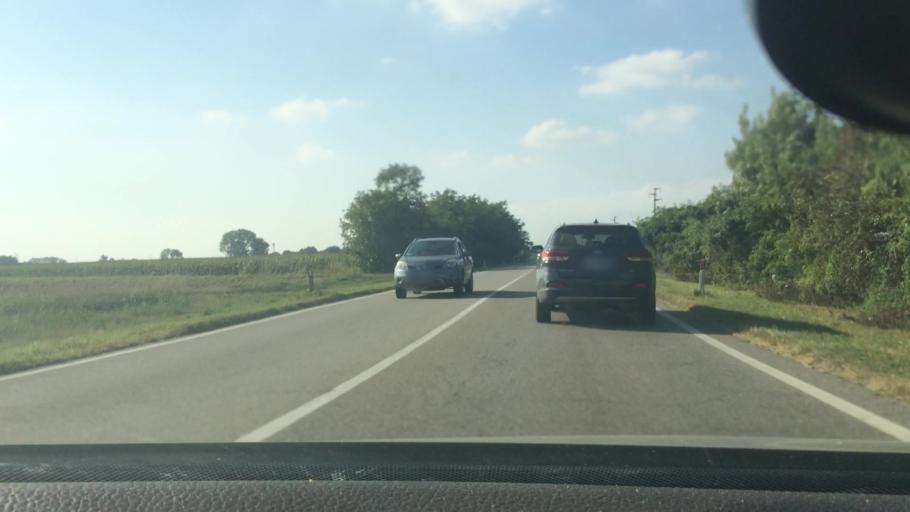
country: IT
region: Lombardy
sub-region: Citta metropolitana di Milano
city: Arconate
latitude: 45.5326
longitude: 8.8304
